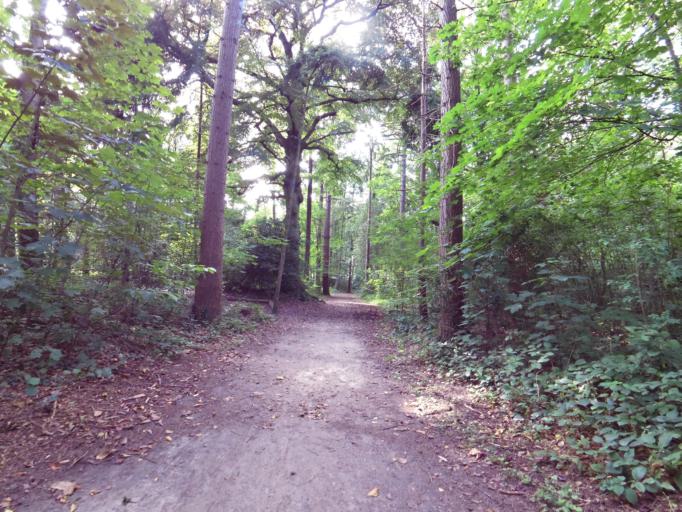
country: BE
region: Flanders
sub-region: Provincie West-Vlaanderen
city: Zedelgem
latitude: 51.1764
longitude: 3.1526
